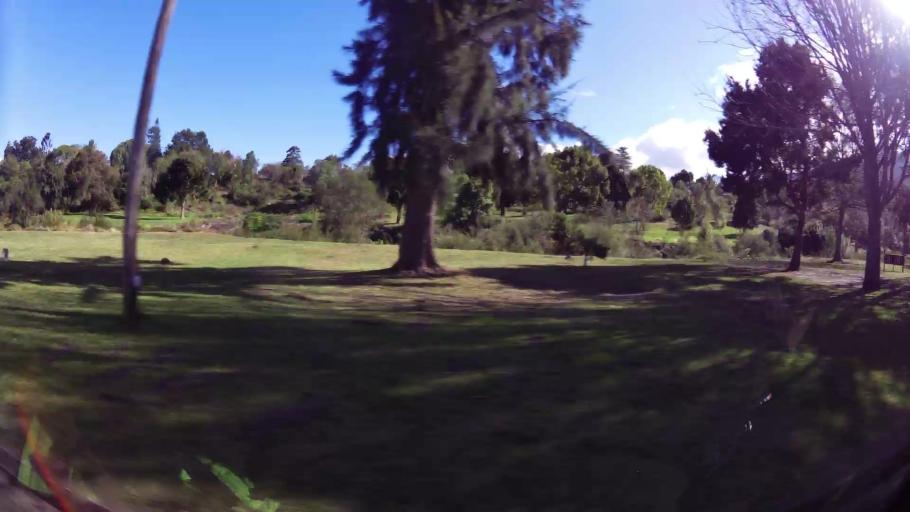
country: ZA
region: Western Cape
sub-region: Eden District Municipality
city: George
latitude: -33.9487
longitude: 22.4573
